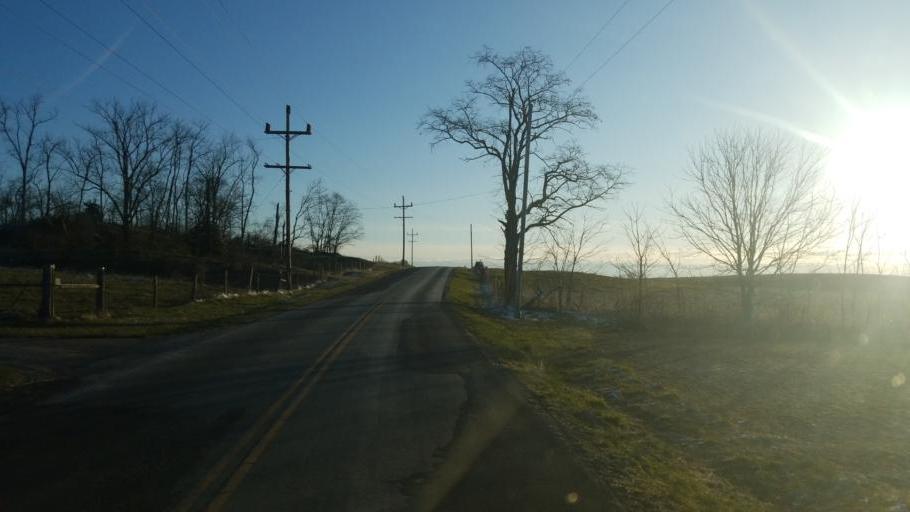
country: US
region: Ohio
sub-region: Highland County
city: Leesburg
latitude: 39.2549
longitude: -83.4681
